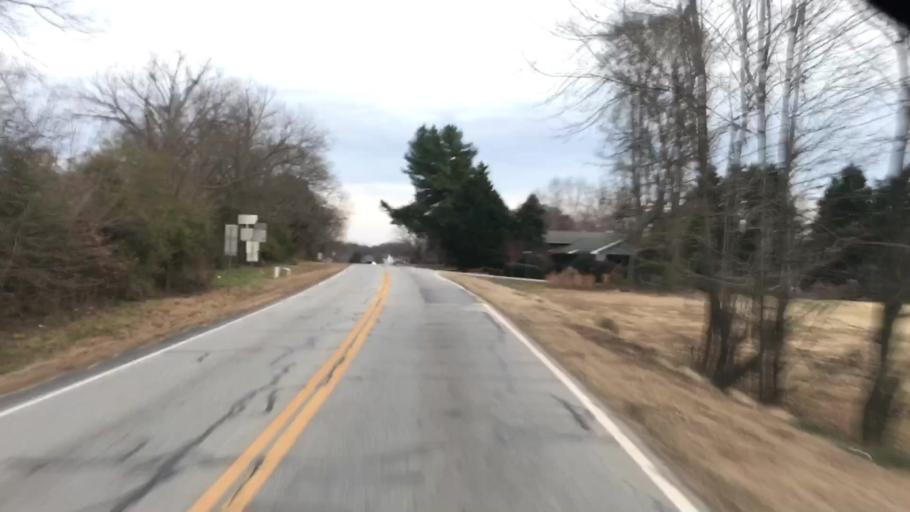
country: US
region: Georgia
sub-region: Barrow County
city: Russell
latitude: 33.9712
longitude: -83.6877
